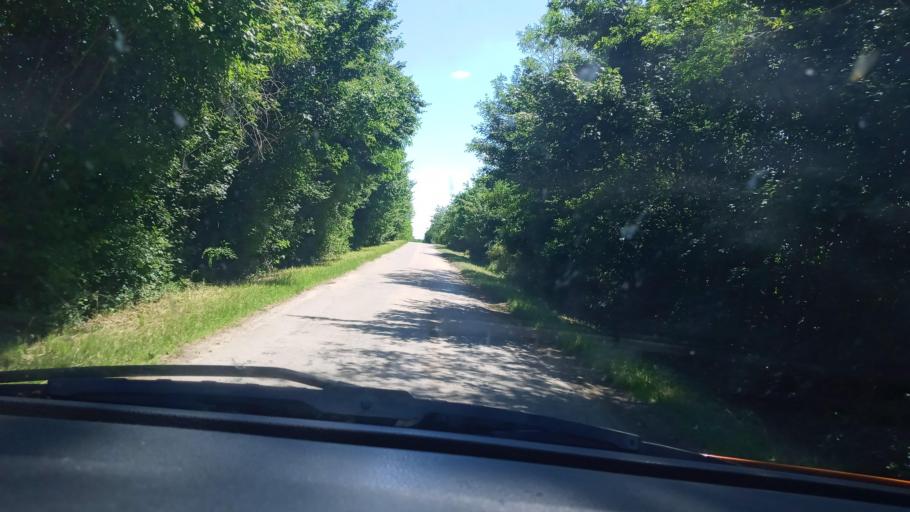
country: HU
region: Somogy
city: Kadarkut
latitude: 46.1851
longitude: 17.7349
